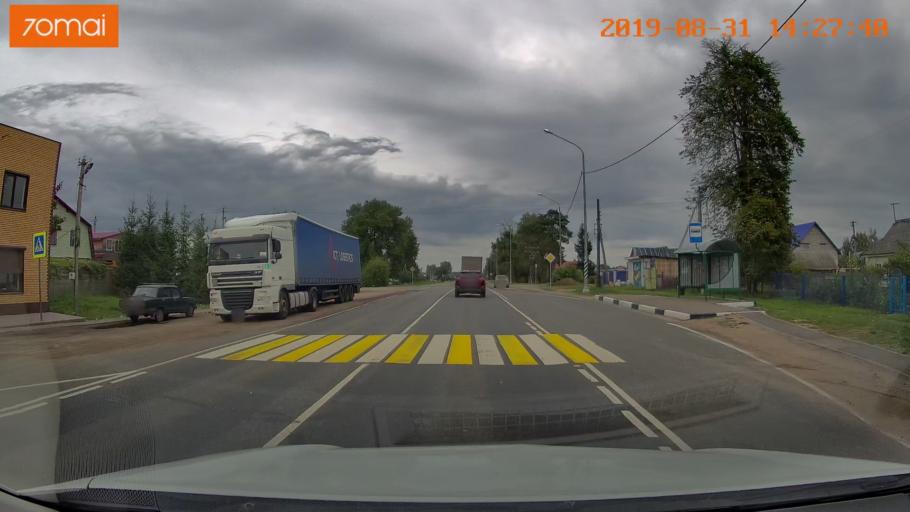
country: RU
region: Smolensk
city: Yekimovichi
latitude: 54.1172
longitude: 33.3030
